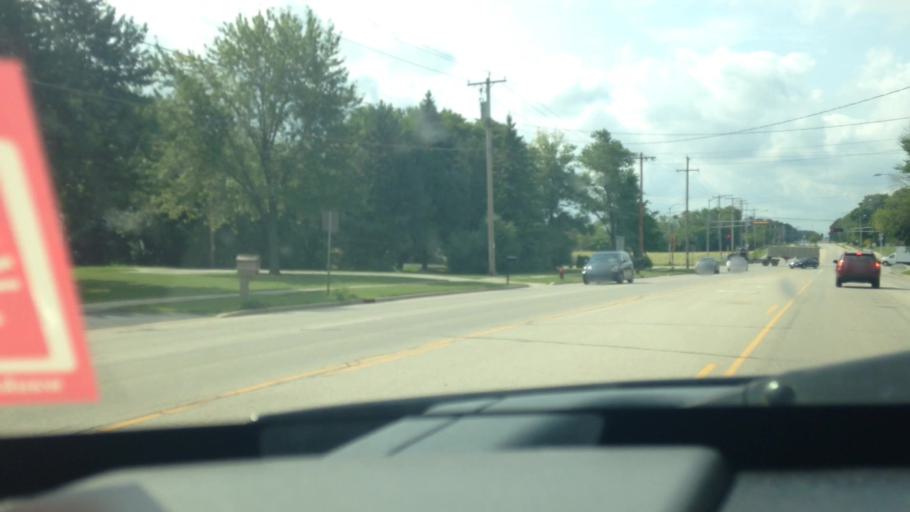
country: US
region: Wisconsin
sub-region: Waukesha County
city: Menomonee Falls
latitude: 43.1497
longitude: -88.1046
